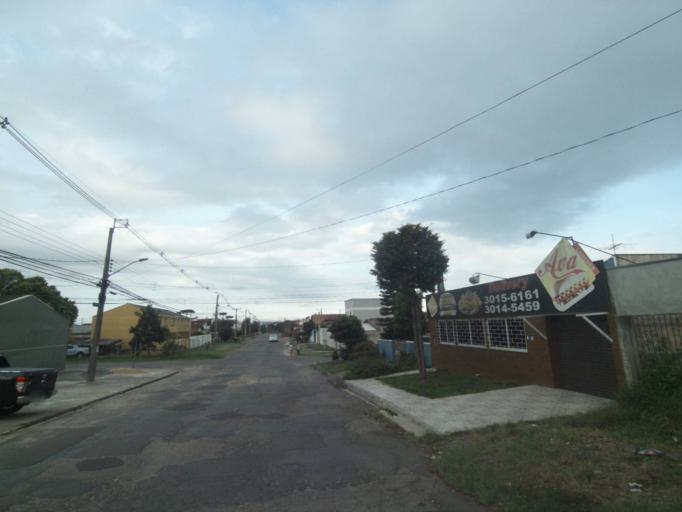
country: BR
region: Parana
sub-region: Pinhais
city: Pinhais
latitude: -25.4141
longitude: -49.2021
